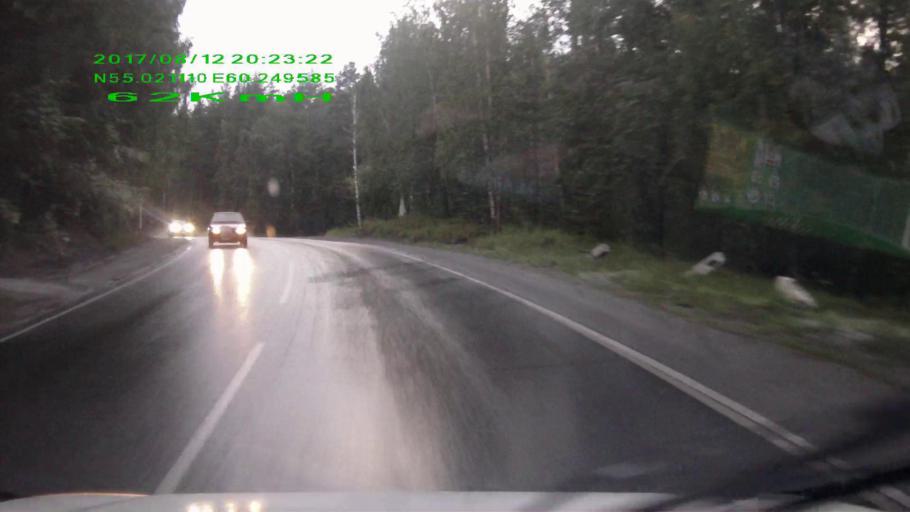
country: RU
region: Chelyabinsk
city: Chebarkul'
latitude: 55.0212
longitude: 60.2495
